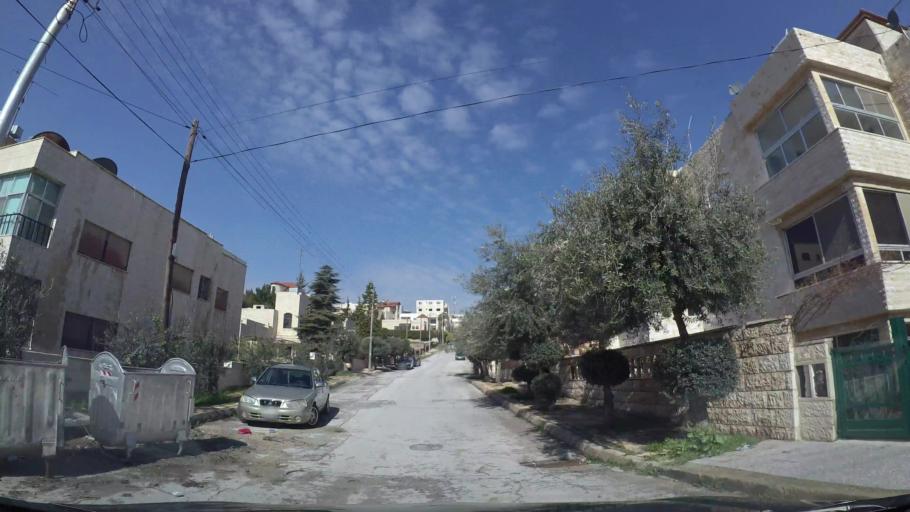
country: JO
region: Amman
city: Al Jubayhah
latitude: 31.9968
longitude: 35.8944
